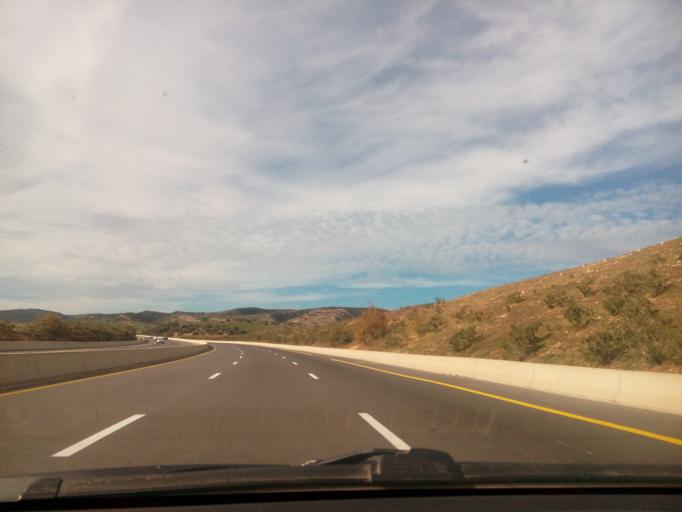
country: DZ
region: Sidi Bel Abbes
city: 'Ain el Berd
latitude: 35.4378
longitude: -0.4426
